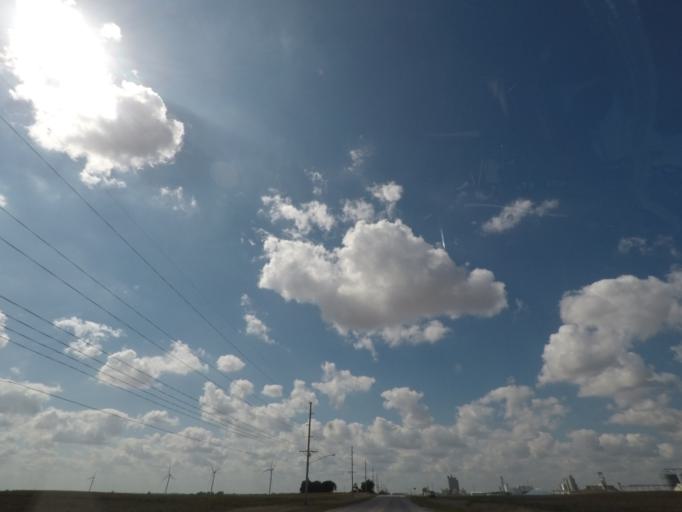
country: US
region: Iowa
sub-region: Story County
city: Nevada
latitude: 42.0231
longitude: -93.4960
